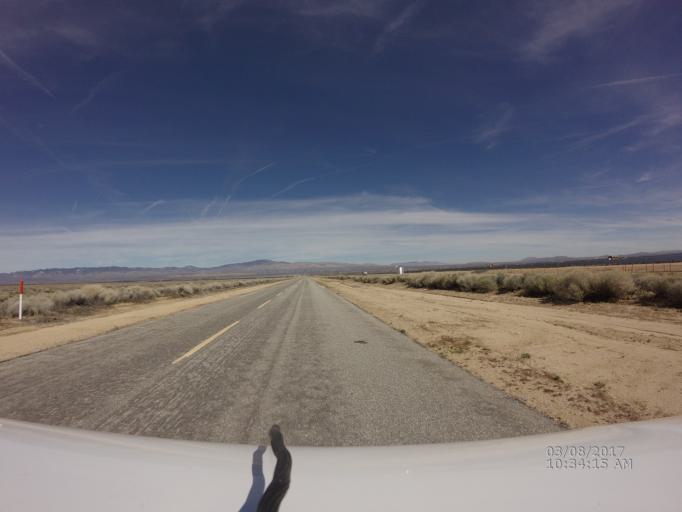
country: US
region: California
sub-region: Los Angeles County
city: Green Valley
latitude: 34.7663
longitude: -118.4314
